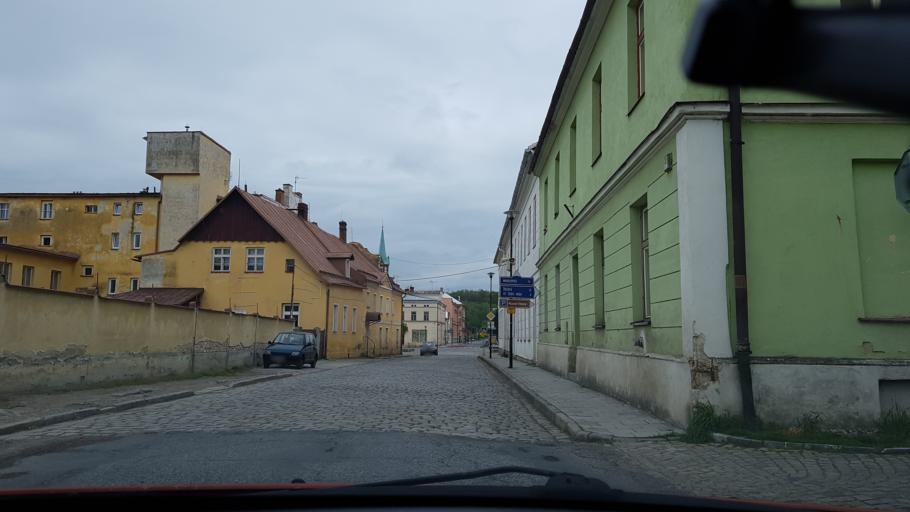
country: CZ
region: Olomoucky
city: Vidnava
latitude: 50.3730
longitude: 17.1848
